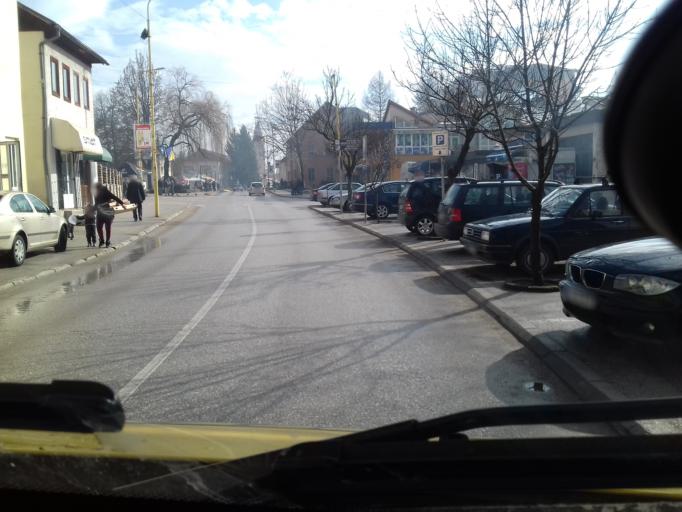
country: BA
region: Federation of Bosnia and Herzegovina
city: Zepce
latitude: 44.4238
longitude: 18.0358
